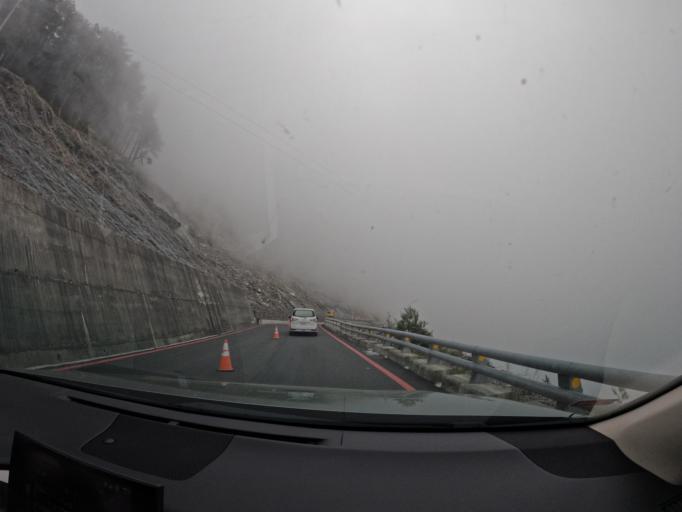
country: TW
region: Taiwan
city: Yujing
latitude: 23.2655
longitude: 120.9668
